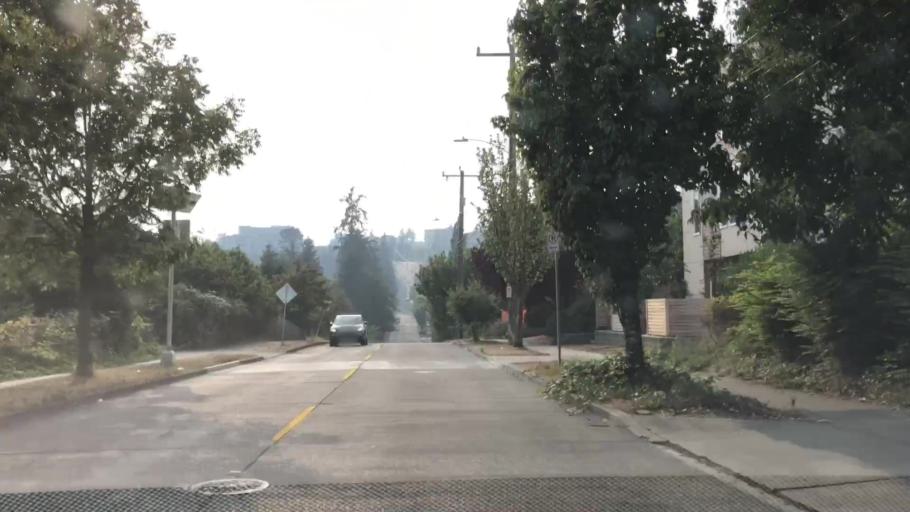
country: US
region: Washington
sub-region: King County
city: White Center
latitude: 47.5648
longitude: -122.3656
